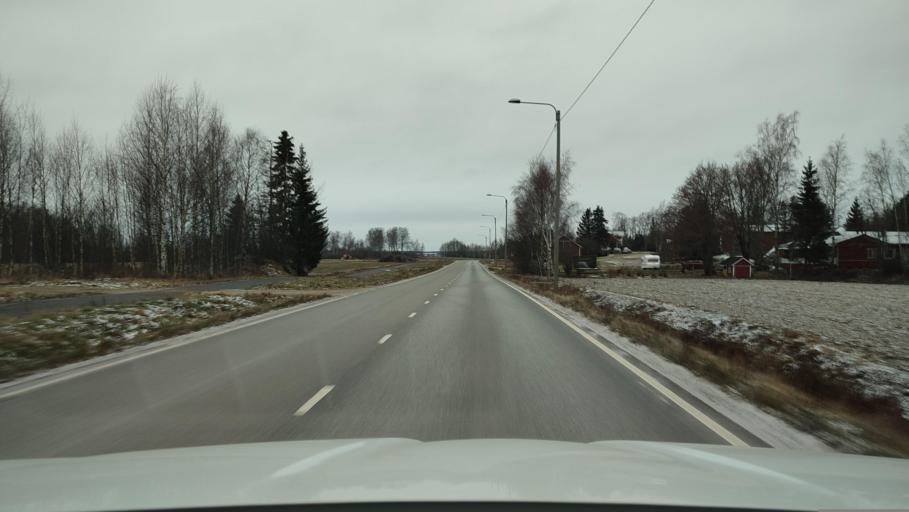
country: FI
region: Ostrobothnia
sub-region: Vaasa
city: Ristinummi
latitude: 63.0345
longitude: 21.7892
